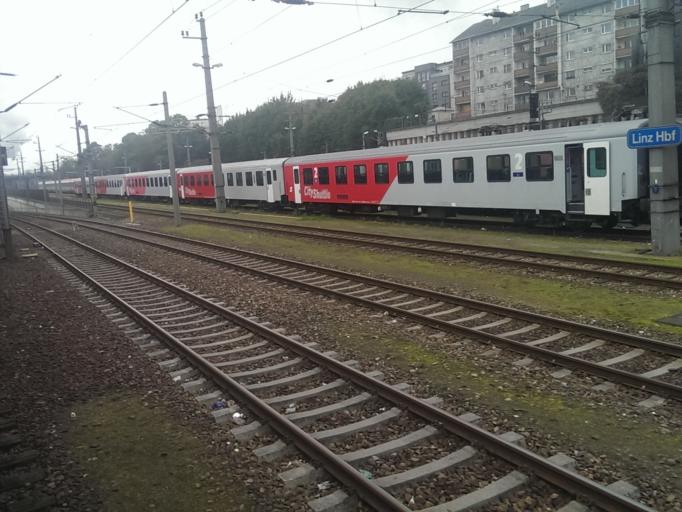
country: AT
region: Upper Austria
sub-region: Linz Stadt
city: Linz
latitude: 48.2865
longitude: 14.2882
